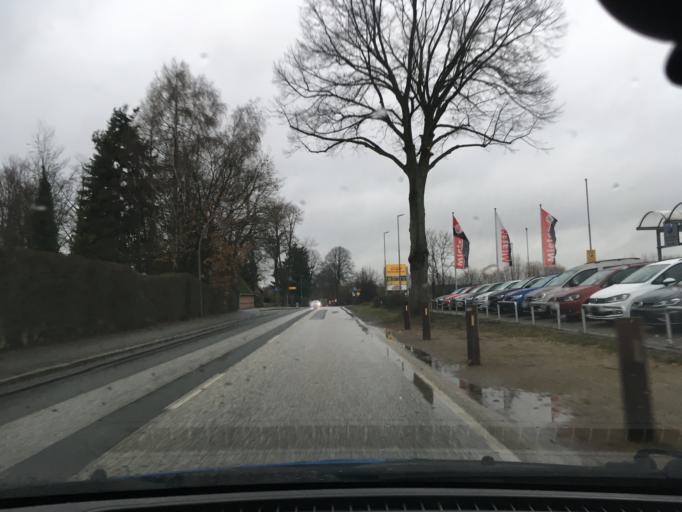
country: DE
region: Schleswig-Holstein
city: Wiershop
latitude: 53.4080
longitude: 10.4461
